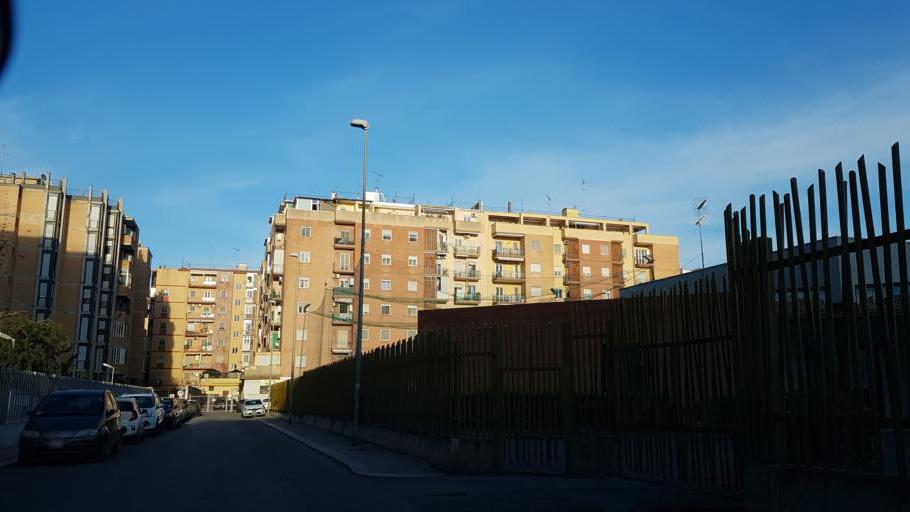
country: IT
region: Apulia
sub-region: Provincia di Brindisi
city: Brindisi
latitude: 40.6277
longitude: 17.9358
